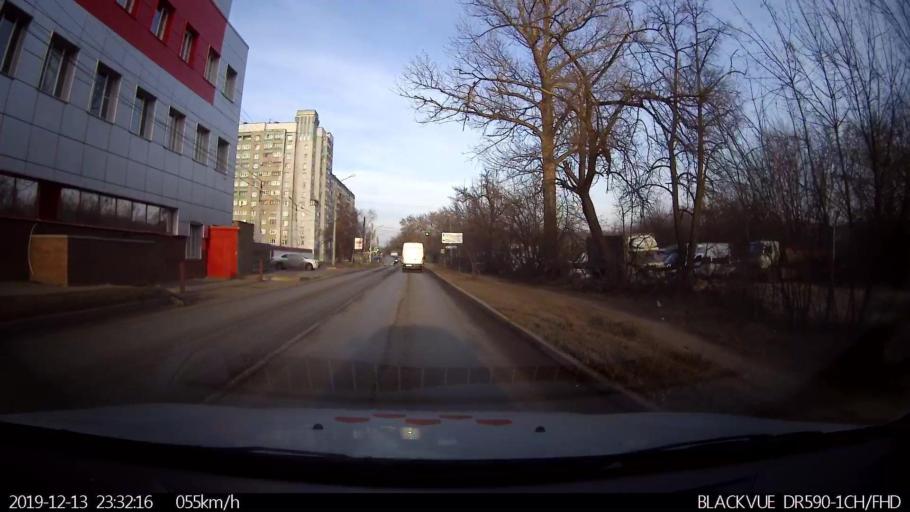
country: RU
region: Nizjnij Novgorod
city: Nizhniy Novgorod
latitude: 56.2731
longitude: 43.9489
